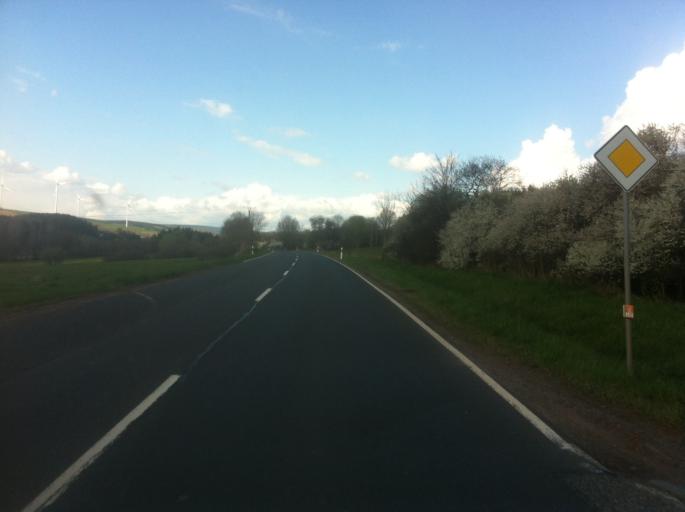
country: DE
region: Rheinland-Pfalz
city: Pronsfeld
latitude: 50.1671
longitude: 6.3451
